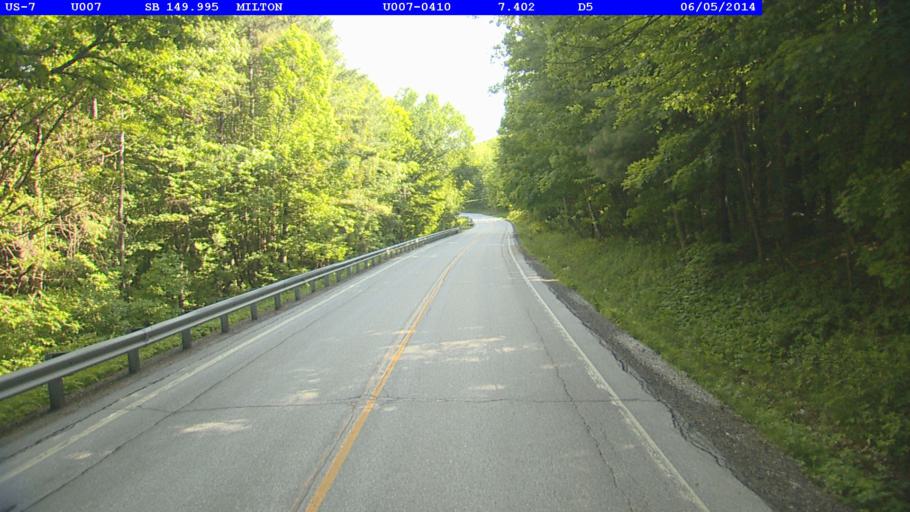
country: US
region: Vermont
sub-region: Chittenden County
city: Milton
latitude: 44.6730
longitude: -73.1114
